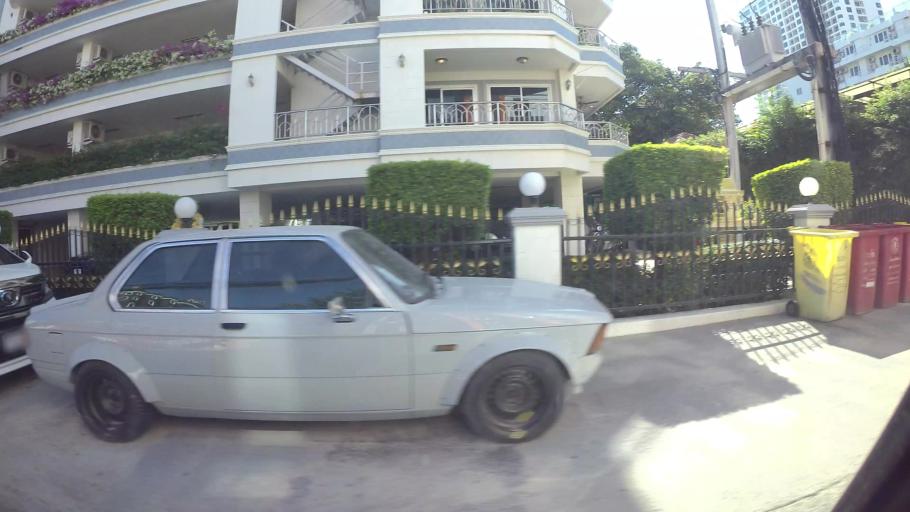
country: TH
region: Chon Buri
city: Phatthaya
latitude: 12.9162
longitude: 100.8614
